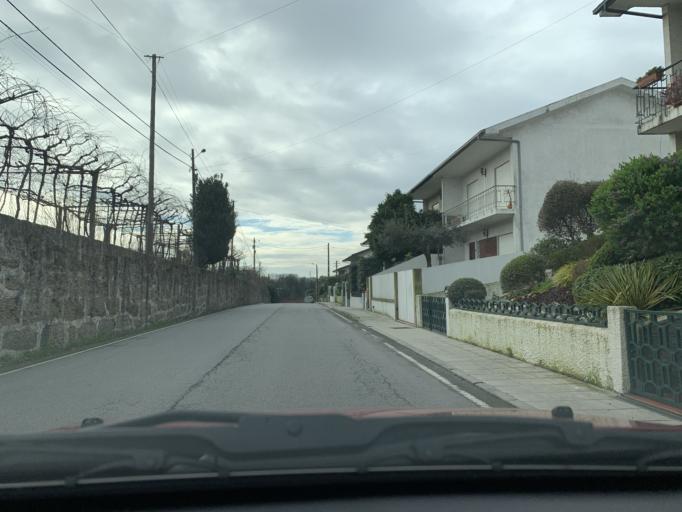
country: PT
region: Braga
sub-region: Vila Nova de Famalicao
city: Vila Nova de Famalicao
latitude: 41.4193
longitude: -8.5006
